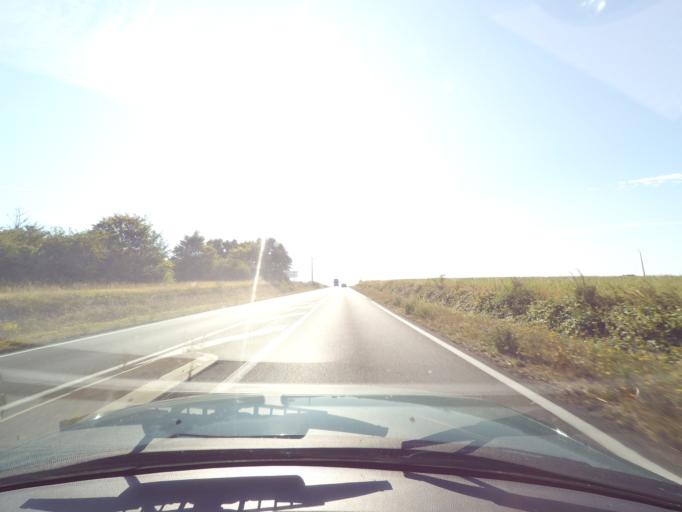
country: FR
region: Poitou-Charentes
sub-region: Departement de la Vienne
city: Cisse
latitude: 46.6402
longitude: 0.2051
